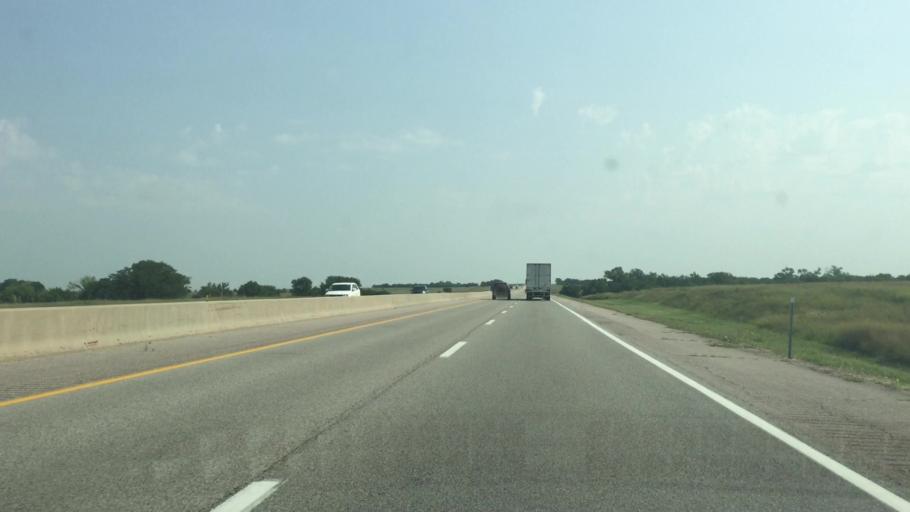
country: US
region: Kansas
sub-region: Butler County
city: El Dorado
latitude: 37.9688
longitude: -96.7237
